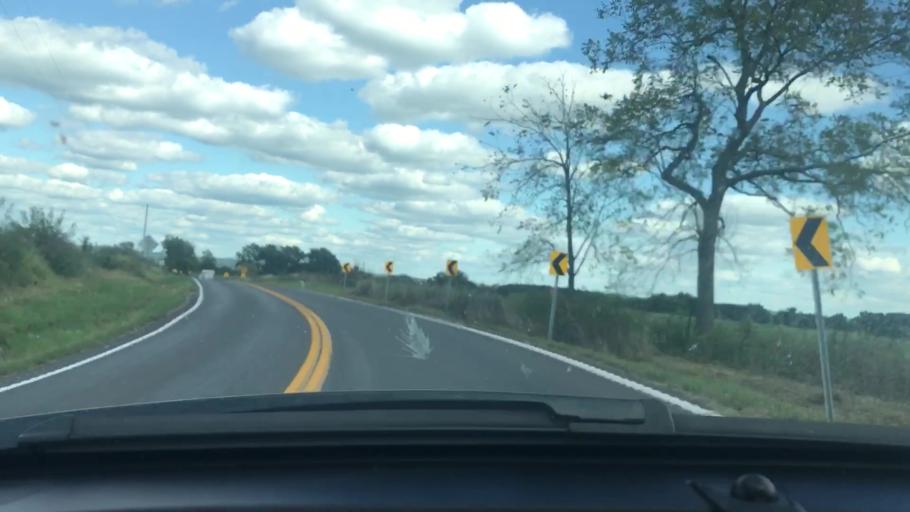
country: US
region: Missouri
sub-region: Wright County
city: Mountain Grove
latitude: 37.1654
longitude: -92.2664
